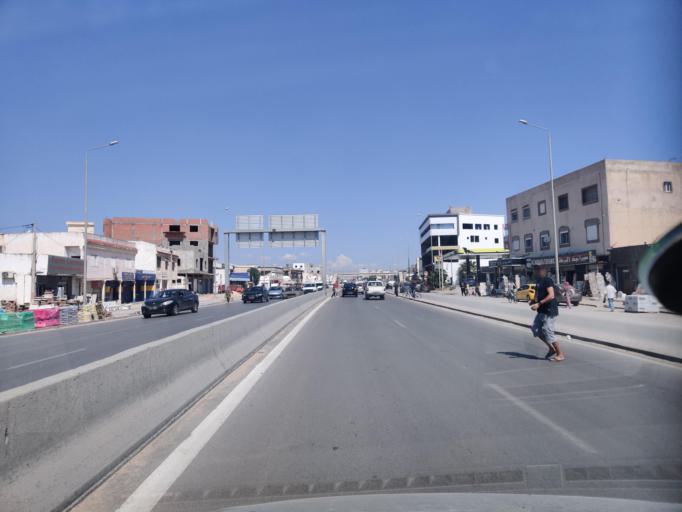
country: TN
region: Manouba
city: Manouba
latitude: 36.7936
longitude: 10.1192
